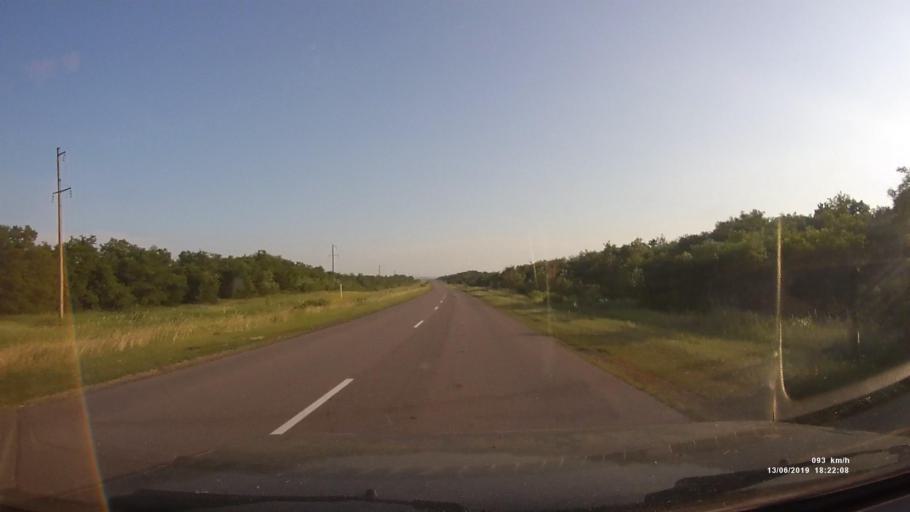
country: RU
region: Rostov
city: Kazanskaya
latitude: 49.8624
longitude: 41.2815
